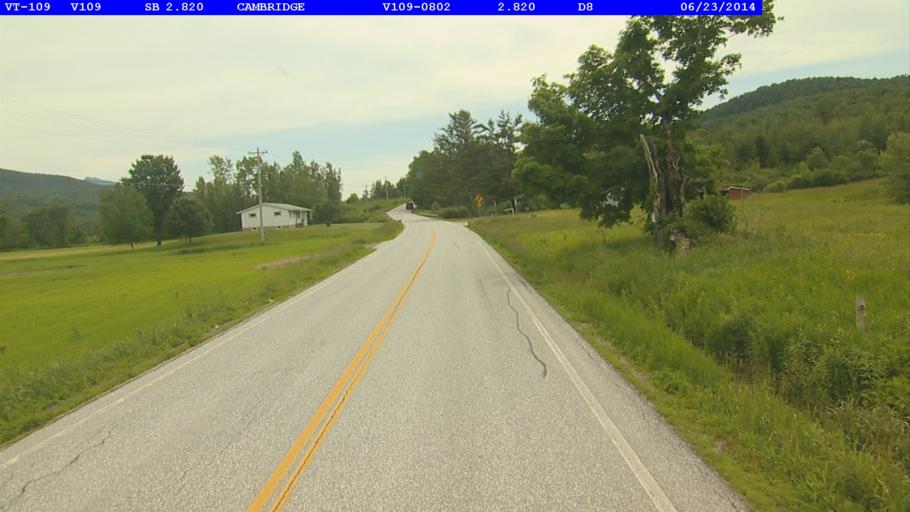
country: US
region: Vermont
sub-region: Lamoille County
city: Johnson
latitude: 44.6760
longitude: -72.7881
